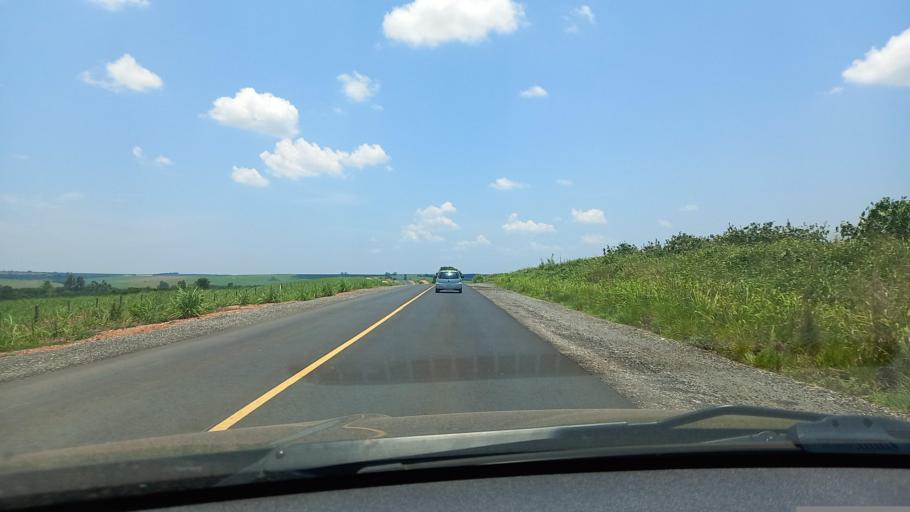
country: BR
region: Sao Paulo
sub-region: Moji-Guacu
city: Mogi-Gaucu
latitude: -22.3665
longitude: -46.8727
